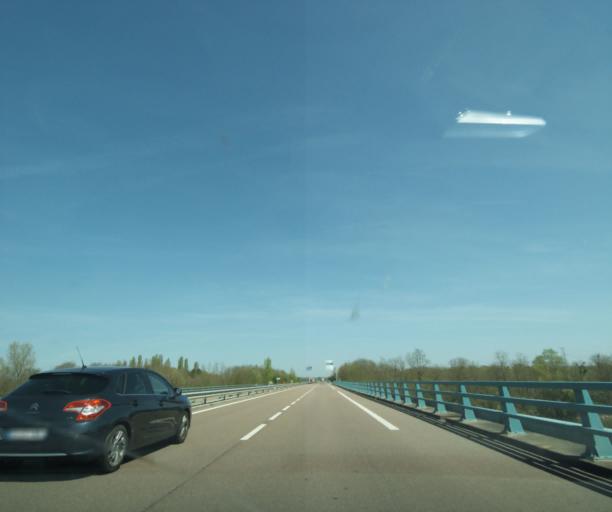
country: FR
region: Bourgogne
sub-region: Departement de la Nievre
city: Saint-Eloi
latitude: 46.9748
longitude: 3.1975
